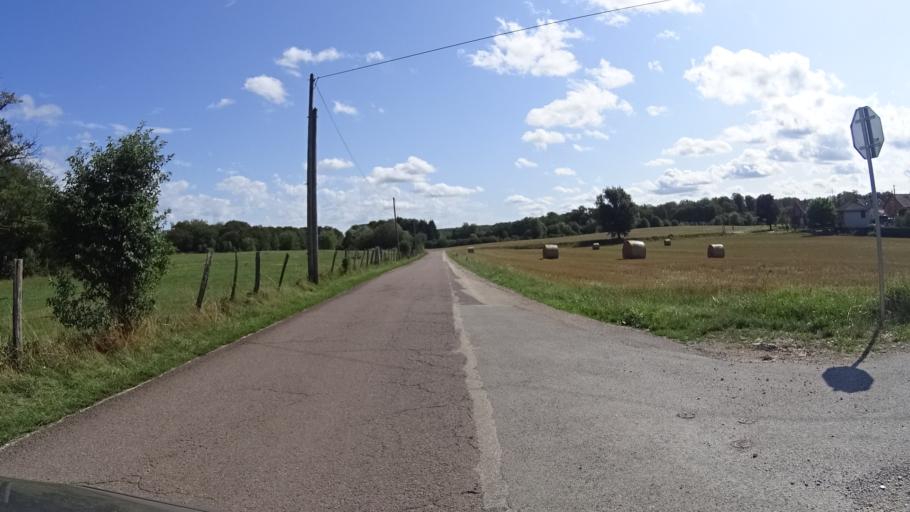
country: FR
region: Franche-Comte
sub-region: Departement du Doubs
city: Saone
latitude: 47.2093
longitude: 6.1105
